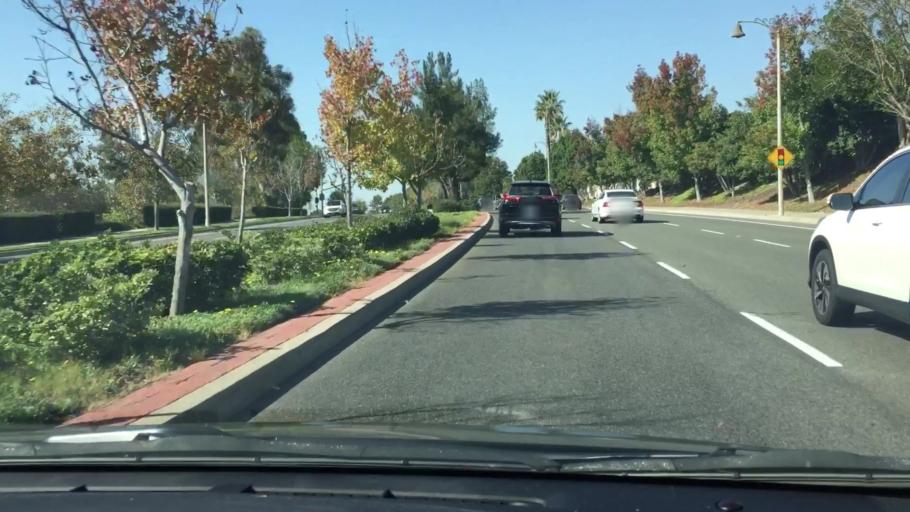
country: US
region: California
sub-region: Orange County
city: Rancho Santa Margarita
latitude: 33.6465
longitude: -117.6259
